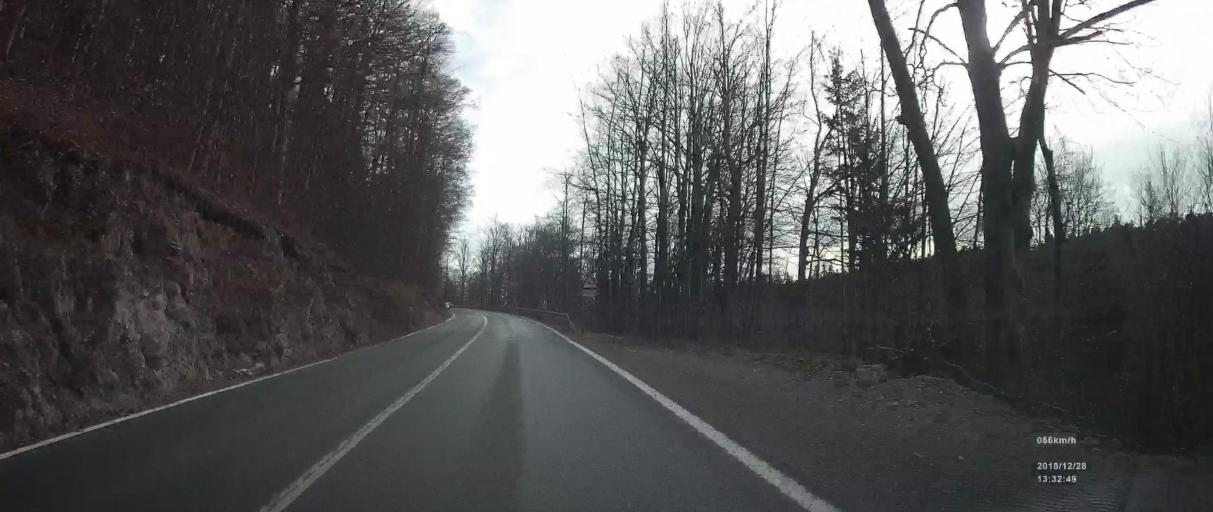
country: HR
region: Primorsko-Goranska
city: Hreljin
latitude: 45.3438
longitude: 14.6695
